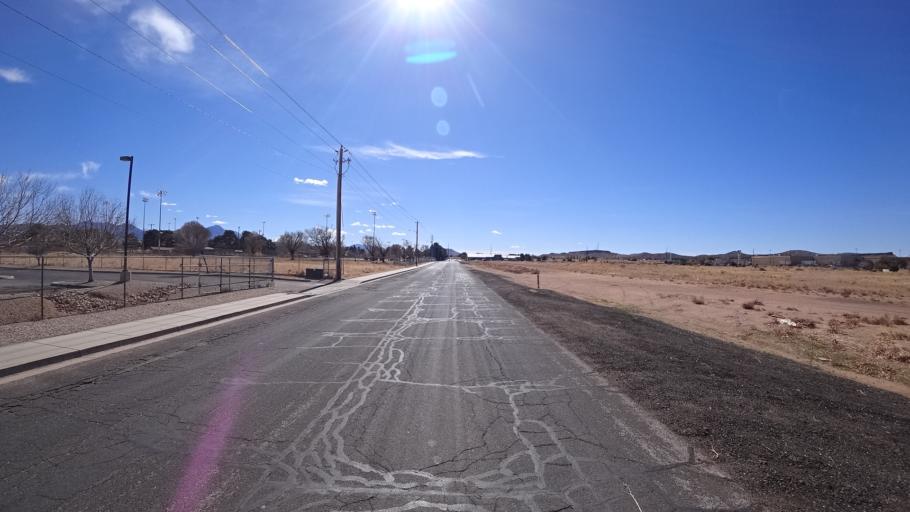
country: US
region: Arizona
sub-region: Mohave County
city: Kingman
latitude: 35.2229
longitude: -114.0292
